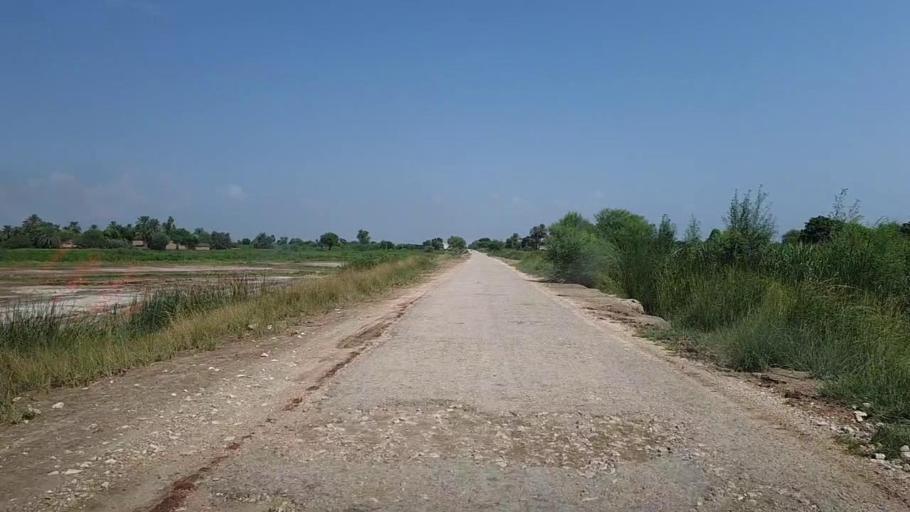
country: PK
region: Sindh
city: Bhiria
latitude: 26.8897
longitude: 68.2290
